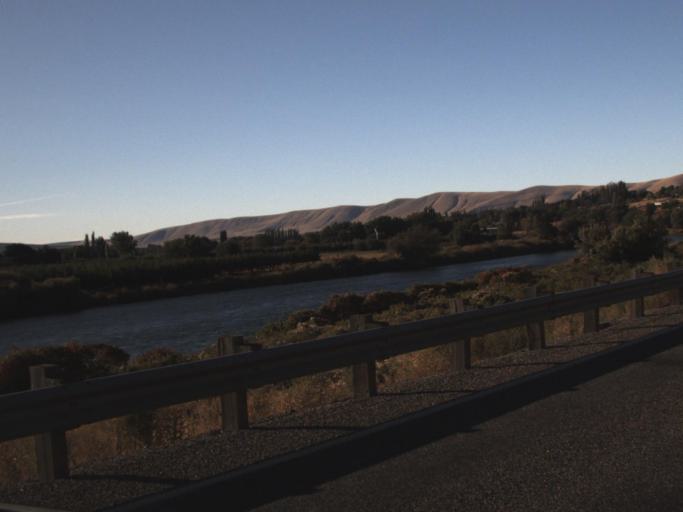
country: US
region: Washington
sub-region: Benton County
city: Benton City
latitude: 46.3309
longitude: -119.4918
